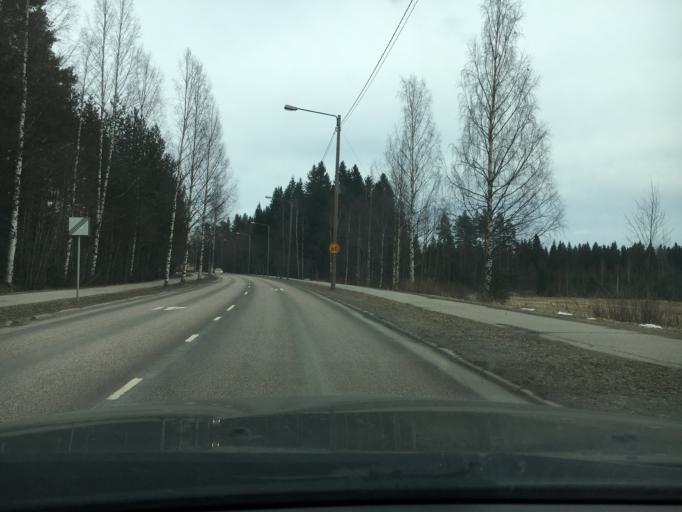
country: FI
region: Central Finland
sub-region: AEaenekoski
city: Konnevesi
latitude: 62.6265
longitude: 26.2994
